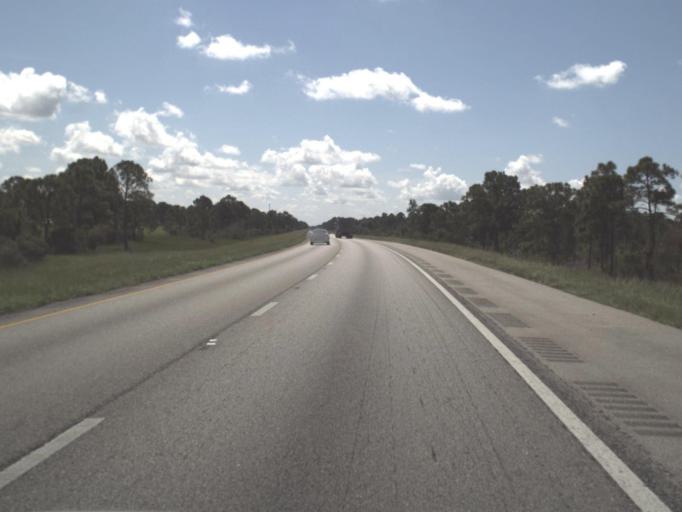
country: US
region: Florida
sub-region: Charlotte County
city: Charlotte Park
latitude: 26.8396
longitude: -81.9652
